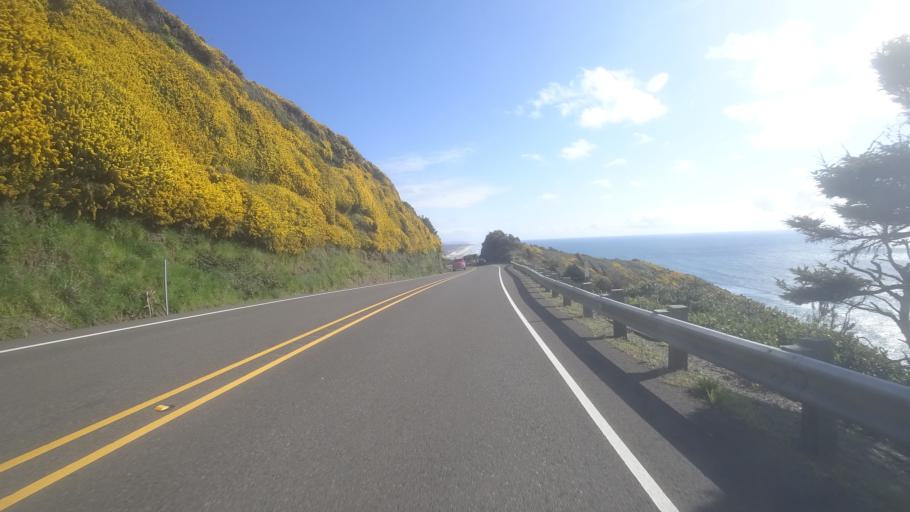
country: US
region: Oregon
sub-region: Lane County
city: Florence
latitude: 44.1119
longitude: -124.1234
